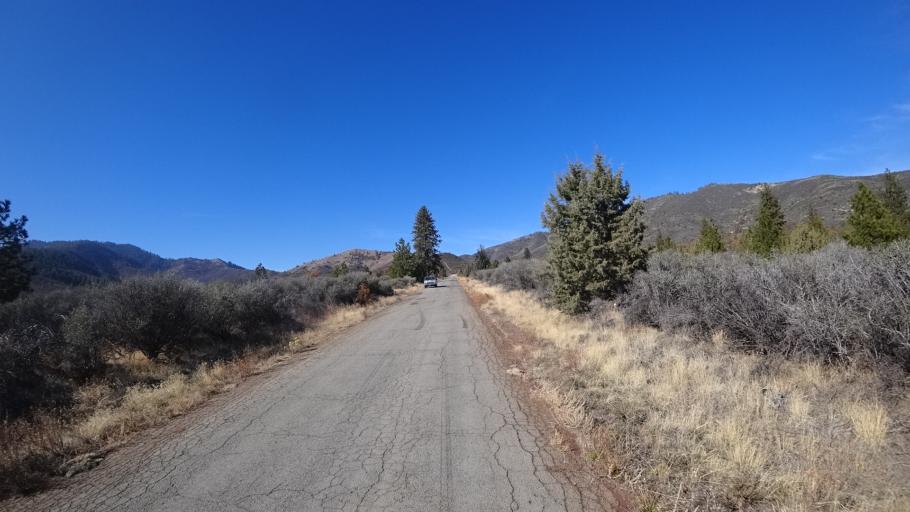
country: US
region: California
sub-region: Siskiyou County
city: Yreka
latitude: 41.7713
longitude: -122.6346
